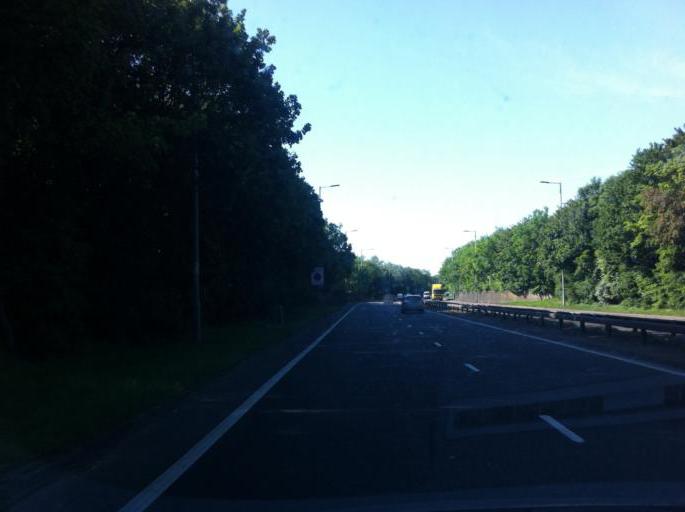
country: GB
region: England
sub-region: Greater London
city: Southall
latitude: 51.5291
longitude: -0.3898
